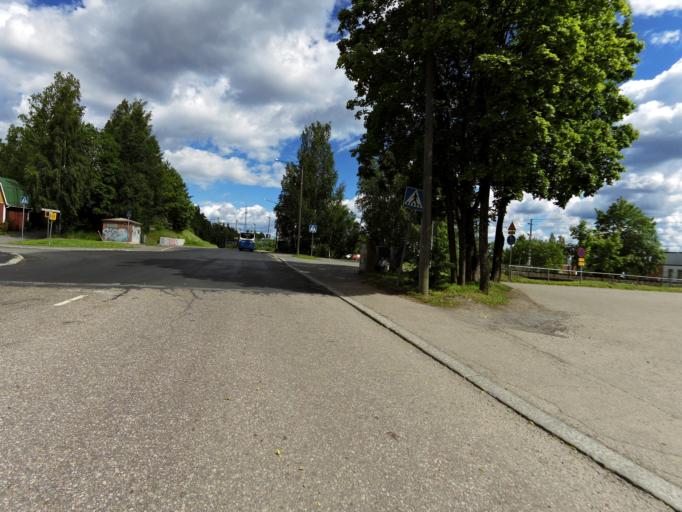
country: FI
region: Pirkanmaa
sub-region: Tampere
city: Pirkkala
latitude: 61.5079
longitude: 23.6622
